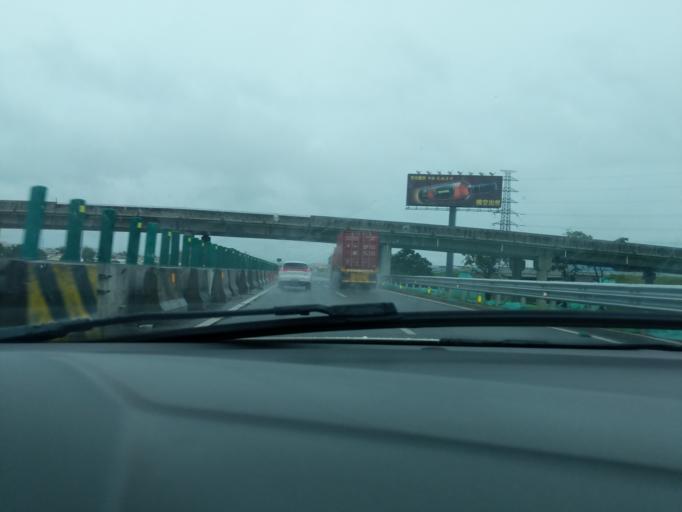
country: CN
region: Guangdong
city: Shuikou
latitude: 22.4712
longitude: 112.7609
